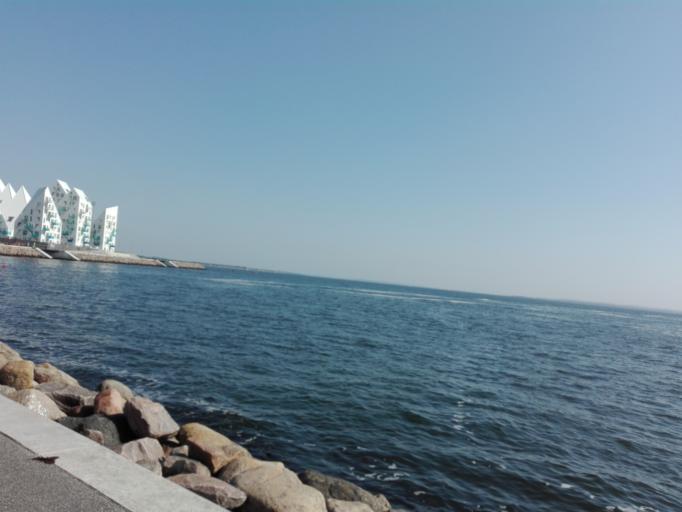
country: DK
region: Central Jutland
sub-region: Arhus Kommune
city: Arhus
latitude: 56.1621
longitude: 10.2290
